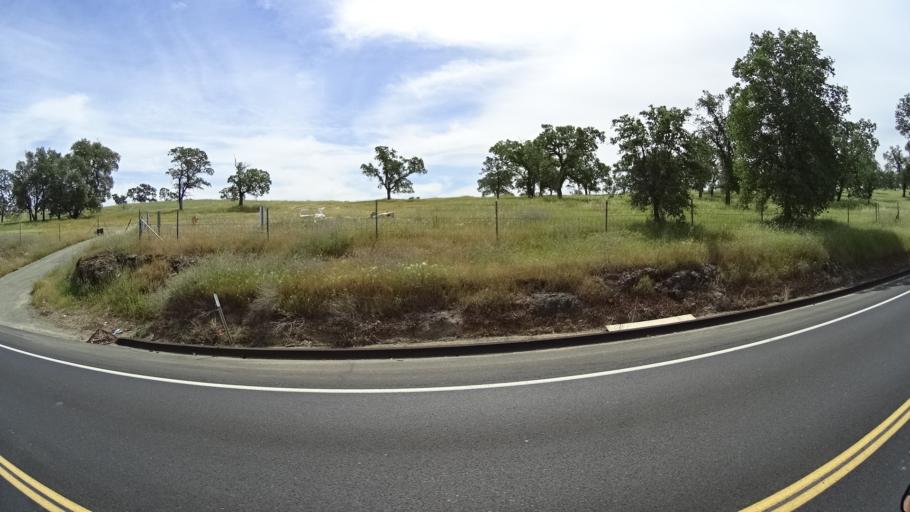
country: US
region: California
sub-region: Placer County
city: Loomis
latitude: 38.8563
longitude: -121.2180
